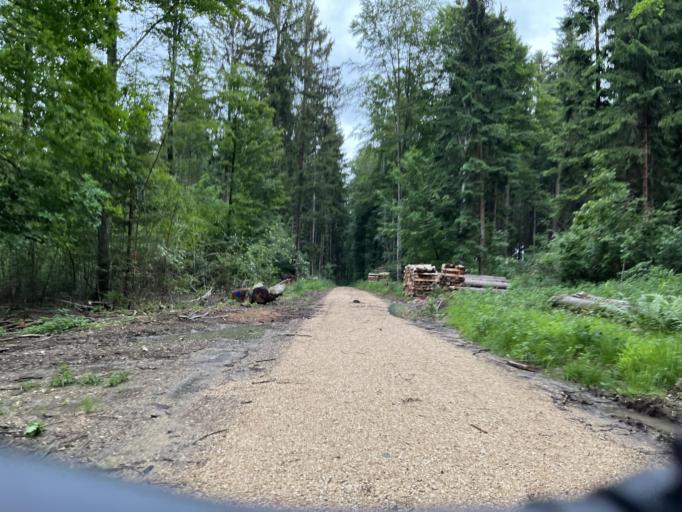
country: DE
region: Baden-Wuerttemberg
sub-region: Tuebingen Region
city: Sigmaringen
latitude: 48.0989
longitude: 9.2453
